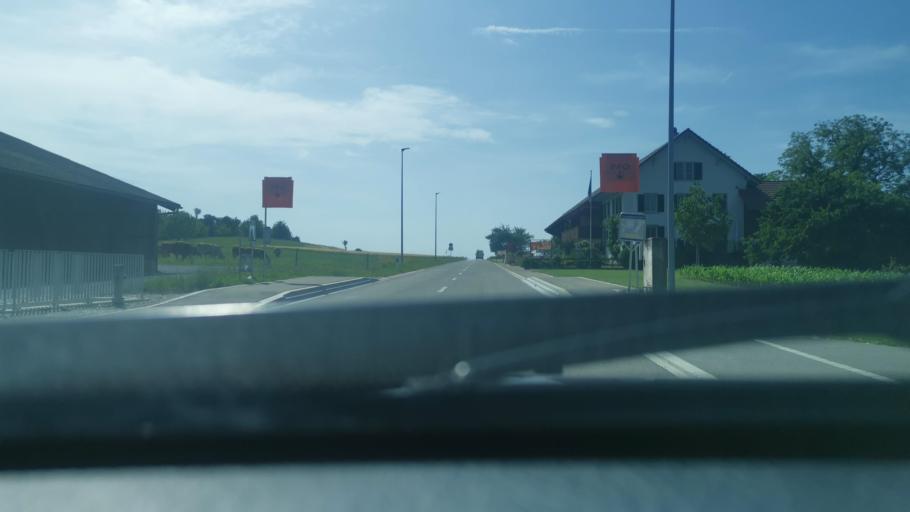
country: CH
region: Zurich
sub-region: Bezirk Winterthur
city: Sulz
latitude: 47.5688
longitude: 8.8008
